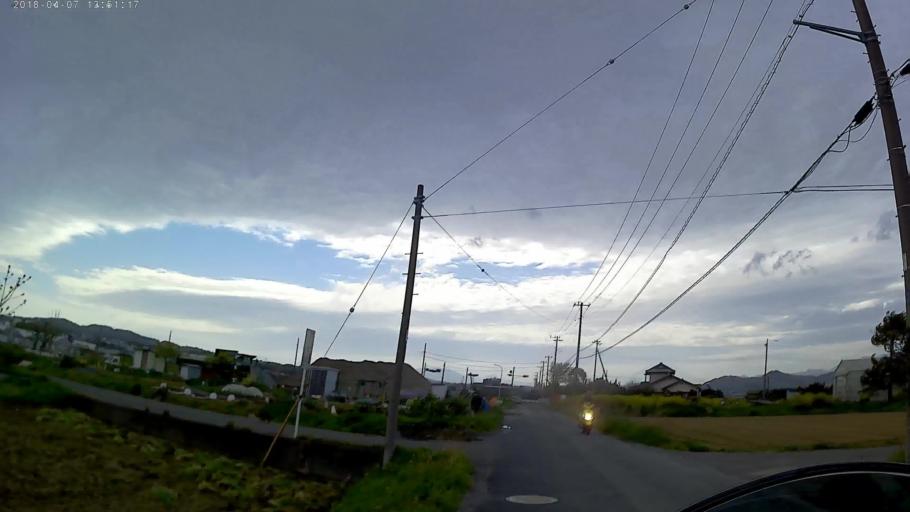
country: JP
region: Kanagawa
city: Isehara
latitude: 35.3664
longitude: 139.3047
